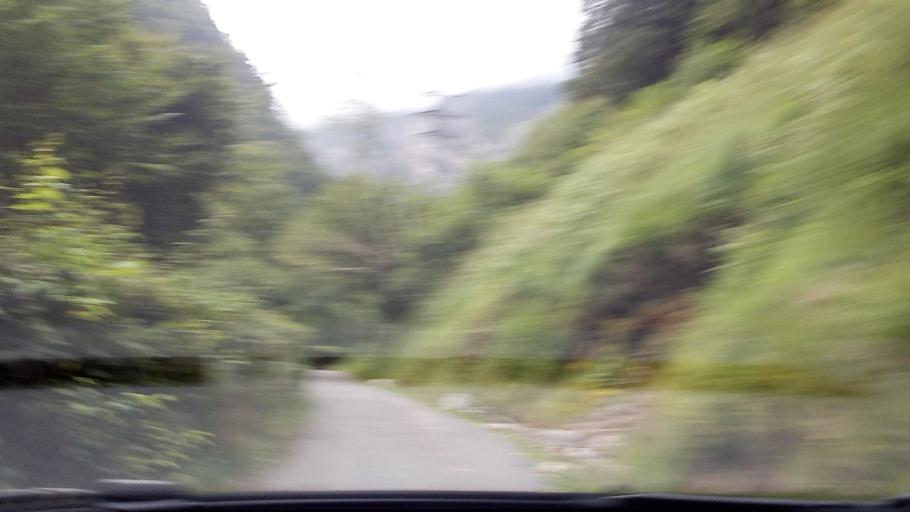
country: FR
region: Aquitaine
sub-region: Departement des Pyrenees-Atlantiques
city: Laruns
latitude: 42.9757
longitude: -0.4302
